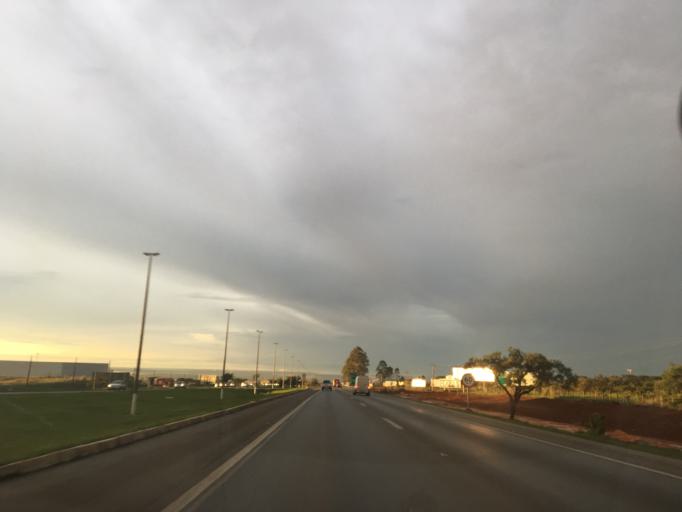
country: BR
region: Goias
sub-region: Luziania
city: Luziania
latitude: -16.0354
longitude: -47.9792
